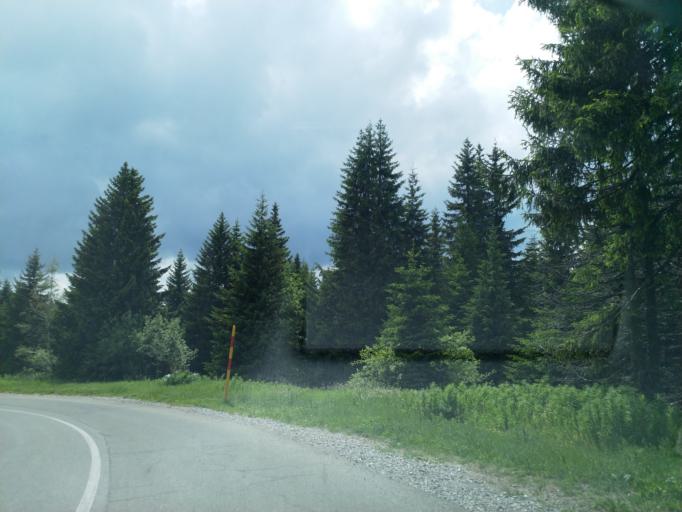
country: XK
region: Mitrovica
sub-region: Komuna e Leposaviqit
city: Leposaviq
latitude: 43.2907
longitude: 20.8149
